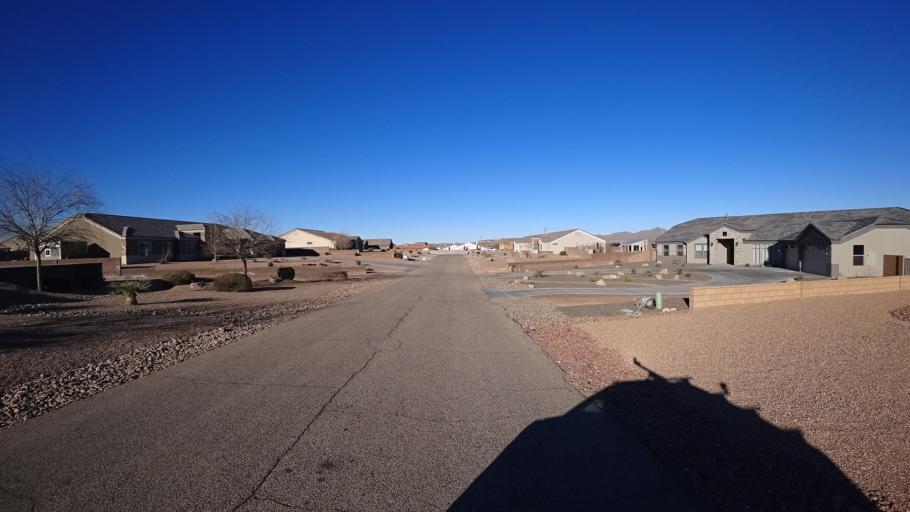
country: US
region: Arizona
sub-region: Mohave County
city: Kingman
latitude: 35.1949
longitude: -114.0007
